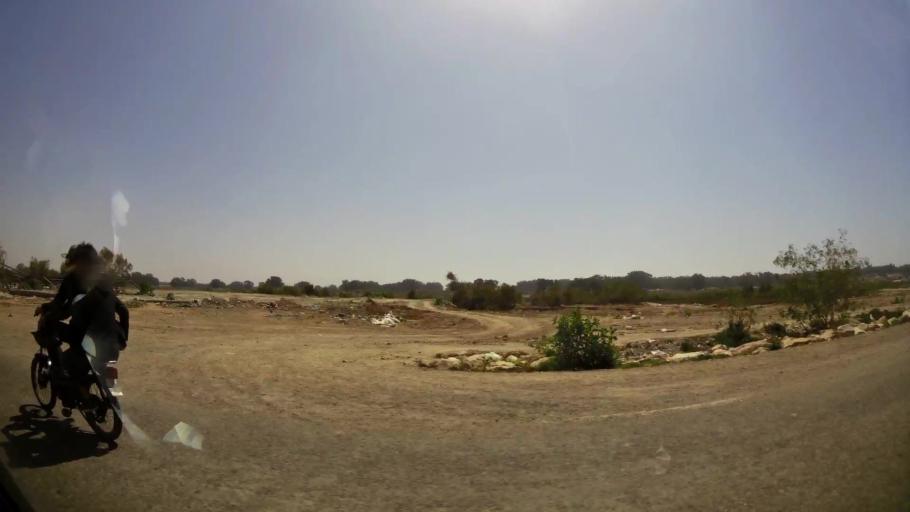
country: MA
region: Souss-Massa-Draa
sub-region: Inezgane-Ait Mellou
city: Inezgane
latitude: 30.3451
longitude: -9.5588
